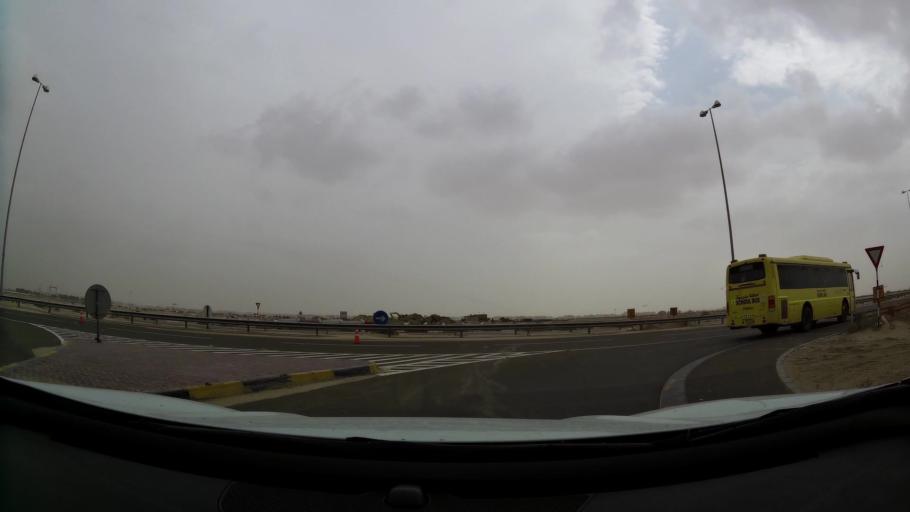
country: AE
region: Abu Dhabi
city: Abu Dhabi
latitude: 24.3688
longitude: 54.6711
